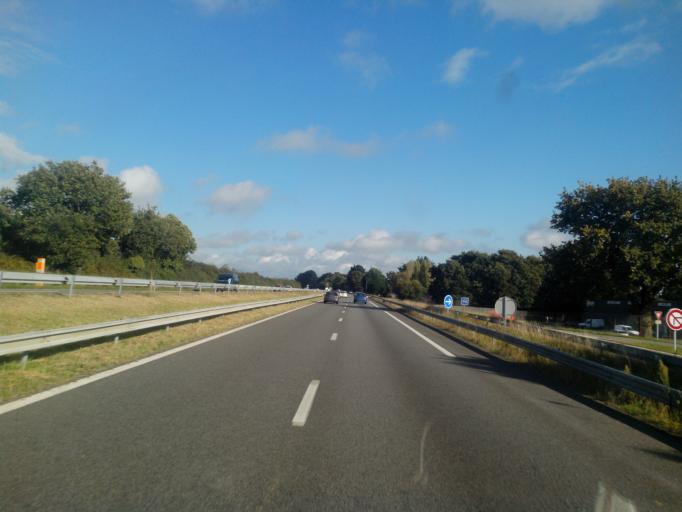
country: FR
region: Brittany
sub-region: Departement du Morbihan
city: Theix
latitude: 47.6343
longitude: -2.6608
